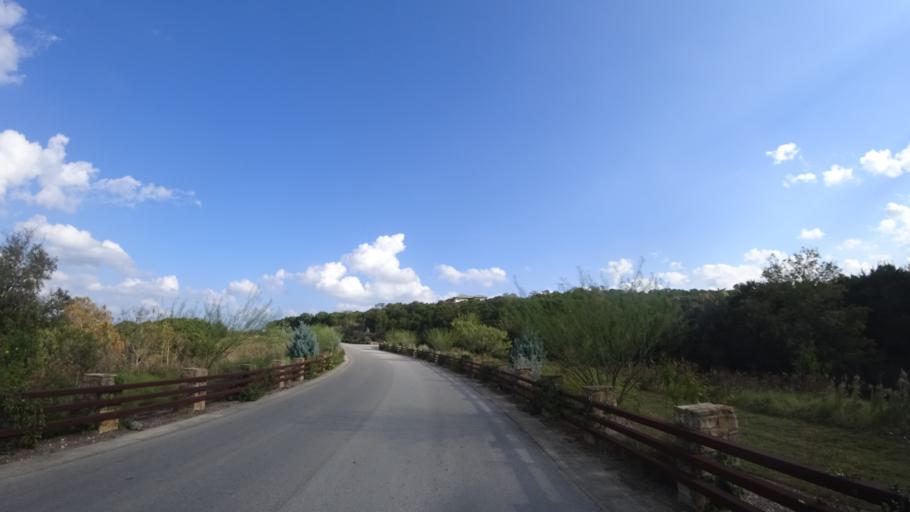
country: US
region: Texas
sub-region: Travis County
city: Barton Creek
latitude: 30.2738
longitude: -97.8833
